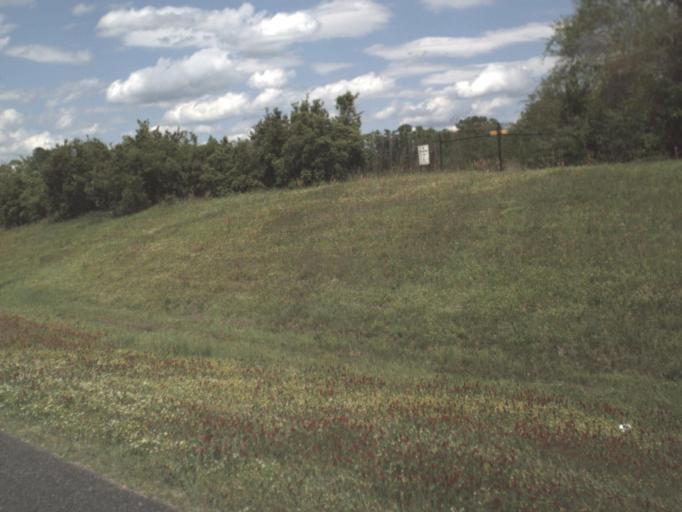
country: US
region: Florida
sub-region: Okaloosa County
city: Crestview
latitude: 30.8039
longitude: -86.5546
